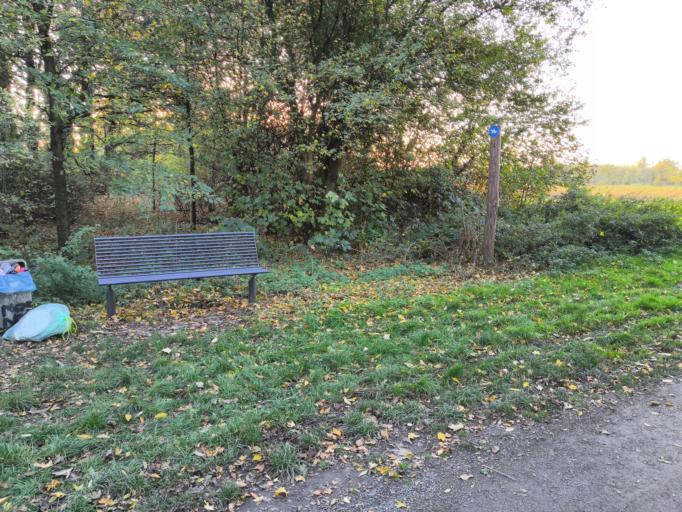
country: DE
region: North Rhine-Westphalia
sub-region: Regierungsbezirk Dusseldorf
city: Hochfeld
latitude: 51.3771
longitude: 6.7087
